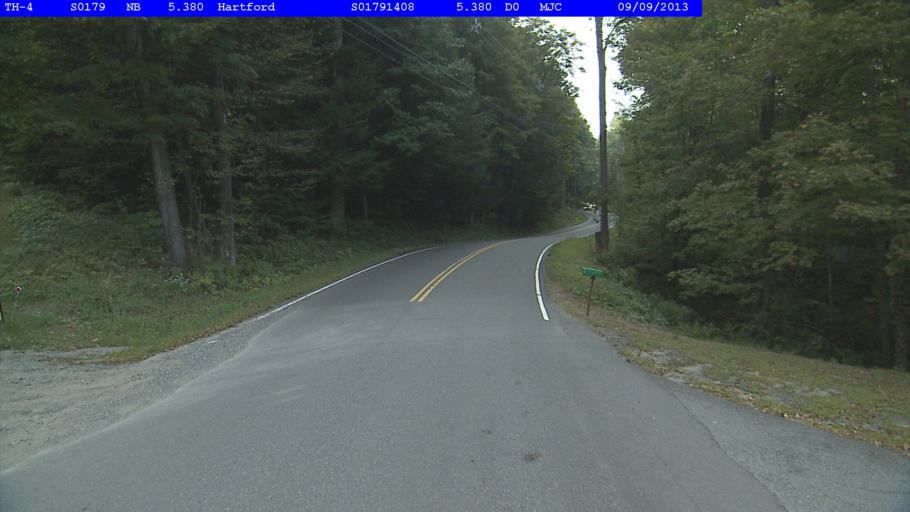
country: US
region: Vermont
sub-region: Windsor County
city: White River Junction
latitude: 43.7057
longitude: -72.4210
